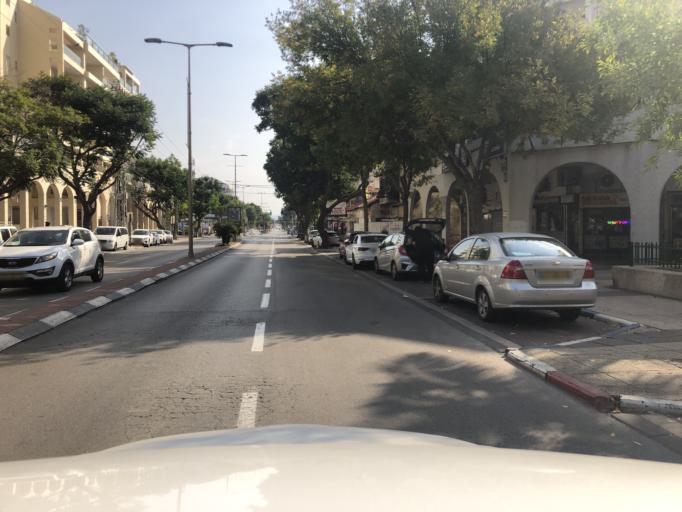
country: IL
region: Central District
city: Kfar Saba
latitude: 32.1743
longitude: 34.9124
